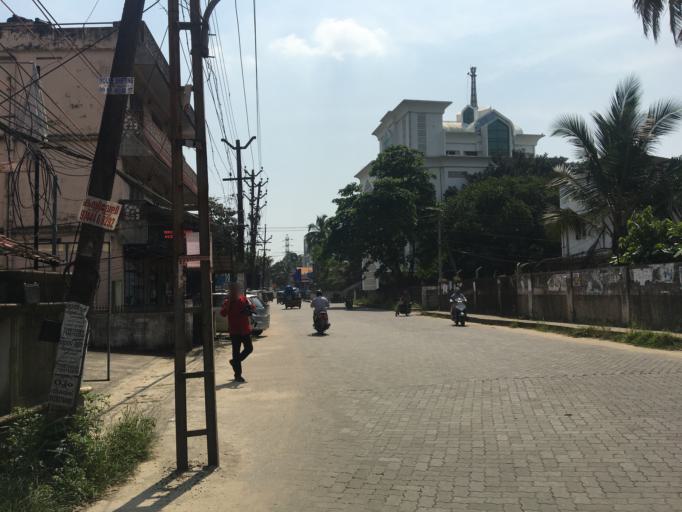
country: IN
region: Kerala
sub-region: Ernakulam
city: Cochin
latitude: 9.9651
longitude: 76.3189
